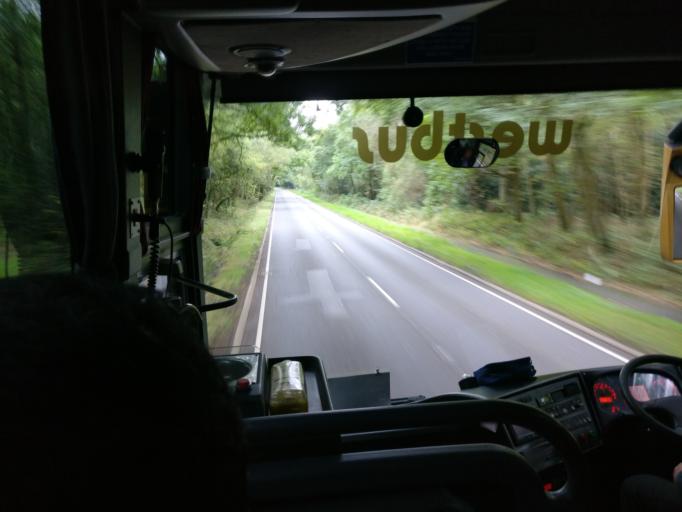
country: GB
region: England
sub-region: Surrey
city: Chobham
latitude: 51.3421
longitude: -0.5923
